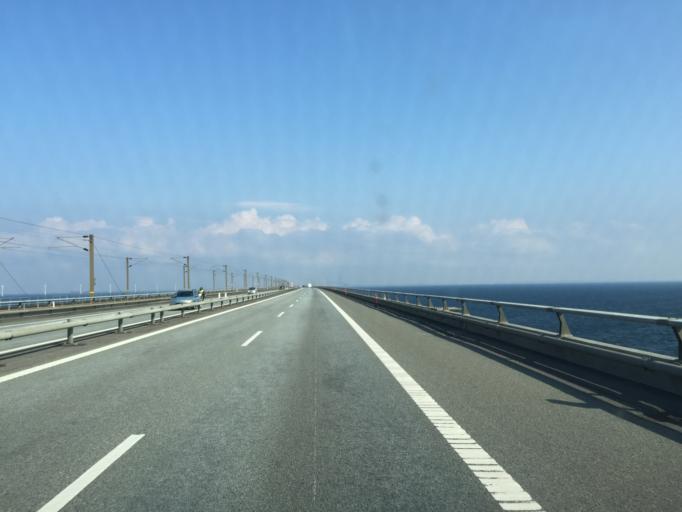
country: DK
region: South Denmark
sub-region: Nyborg Kommune
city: Nyborg
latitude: 55.3081
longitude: 10.8931
